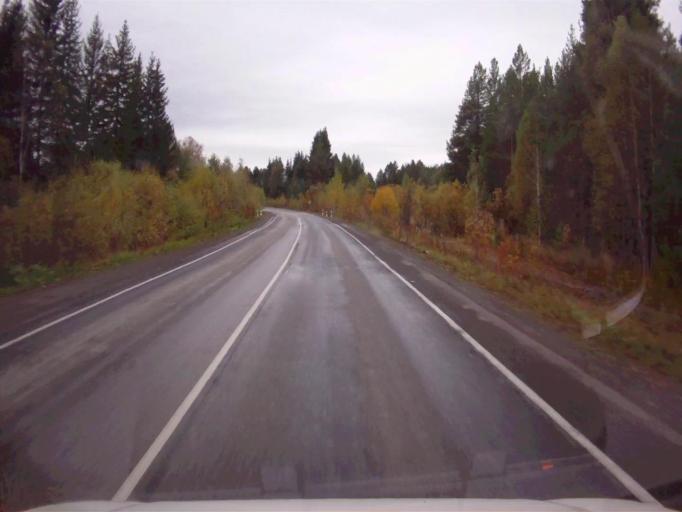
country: RU
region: Chelyabinsk
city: Nyazepetrovsk
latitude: 56.0661
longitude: 59.7004
